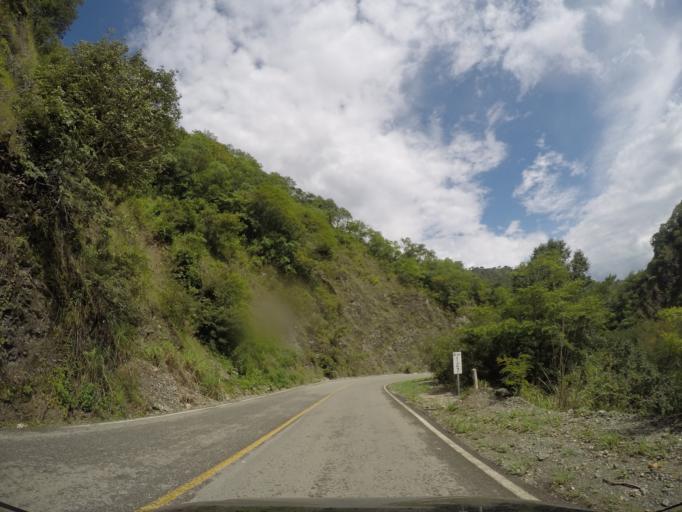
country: MX
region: Oaxaca
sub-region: San Jeronimo Coatlan
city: San Cristobal Honduras
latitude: 16.3672
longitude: -97.0884
